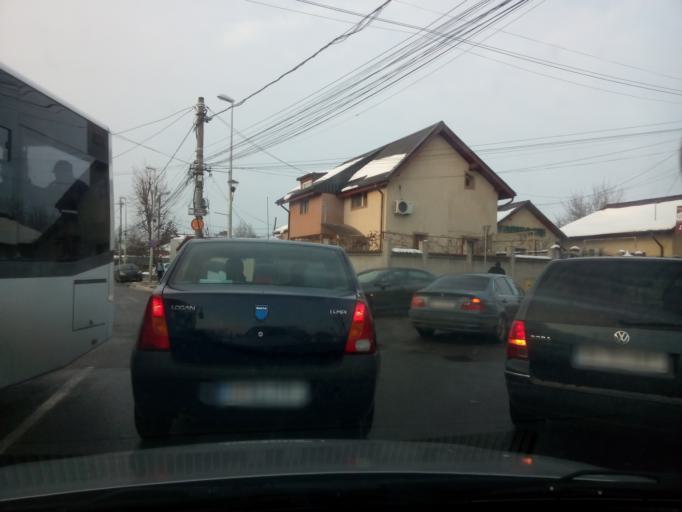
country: RO
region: Ilfov
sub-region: Comuna Pantelimon
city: Pantelimon
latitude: 44.4519
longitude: 26.2050
